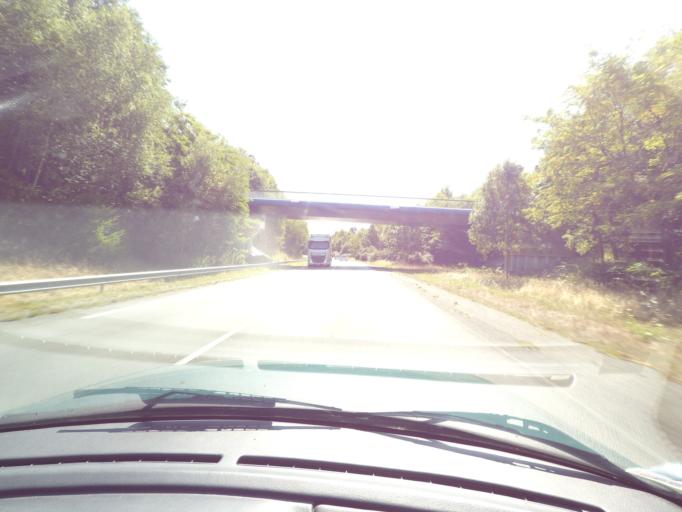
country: FR
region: Limousin
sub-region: Departement de la Haute-Vienne
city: Chaptelat
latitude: 45.8934
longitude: 1.2499
